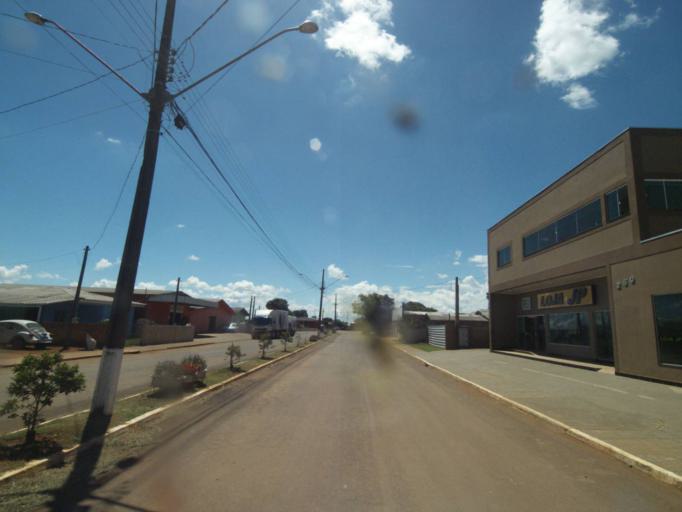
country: BR
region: Parana
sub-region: Pinhao
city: Pinhao
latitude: -25.8344
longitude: -52.0267
